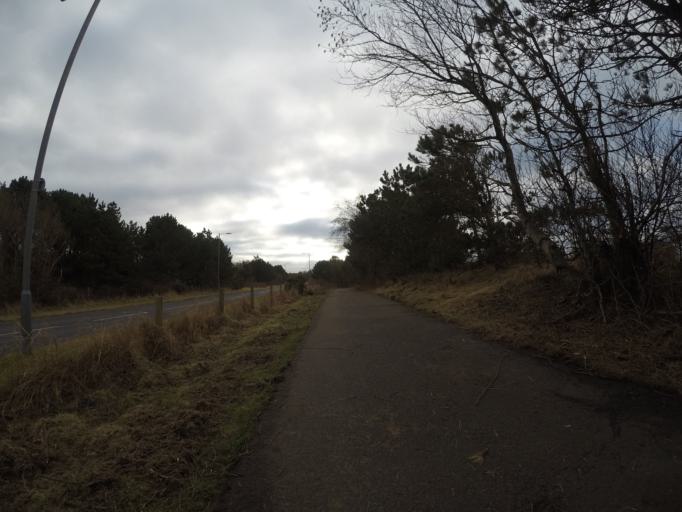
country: GB
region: Scotland
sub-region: North Ayrshire
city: Irvine
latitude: 55.5984
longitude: -4.6774
